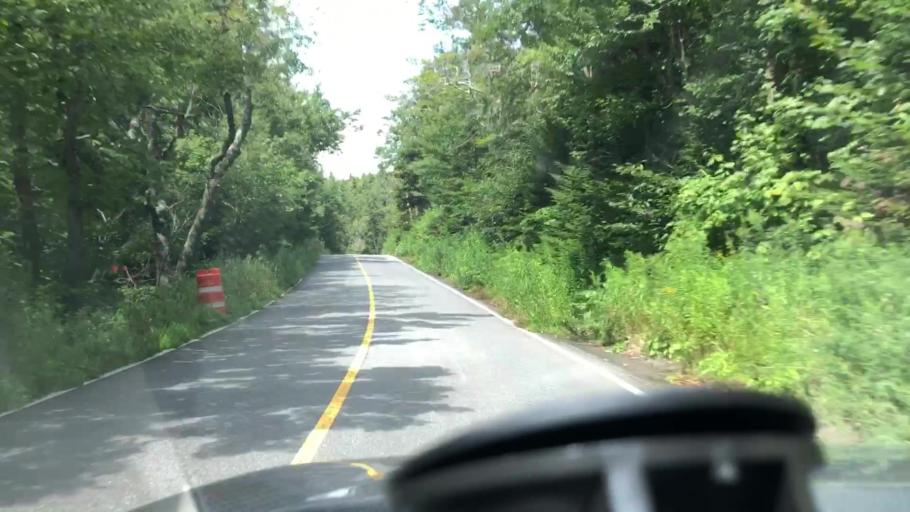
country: US
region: Massachusetts
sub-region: Berkshire County
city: Adams
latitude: 42.6529
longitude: -73.1618
